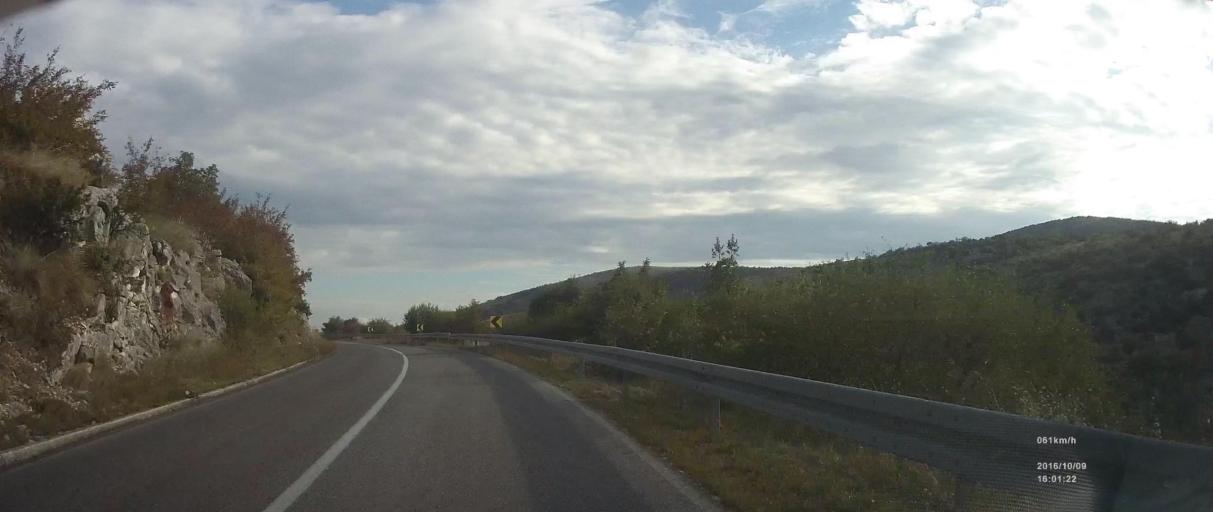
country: HR
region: Splitsko-Dalmatinska
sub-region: Grad Trogir
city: Trogir
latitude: 43.5646
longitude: 16.2455
